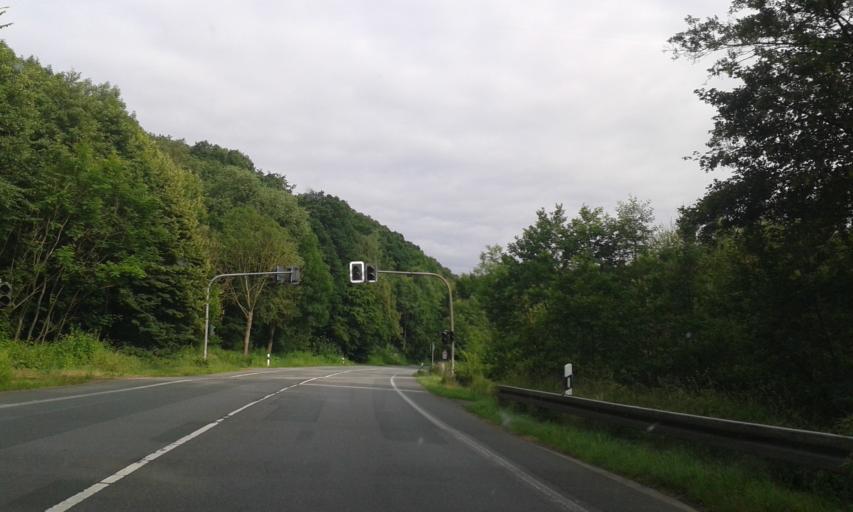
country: DE
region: Lower Saxony
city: Rinteln
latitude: 52.1354
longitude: 9.0866
